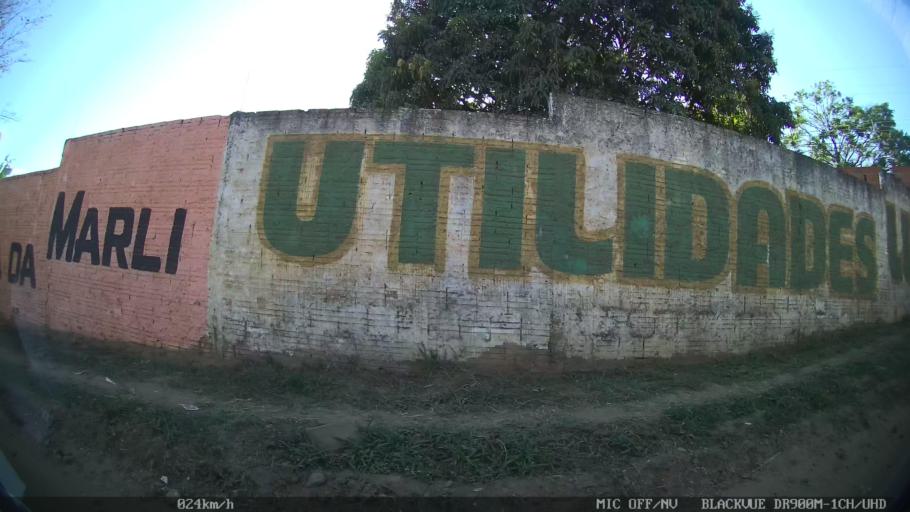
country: BR
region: Sao Paulo
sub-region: Franca
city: Franca
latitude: -20.4811
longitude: -47.4206
